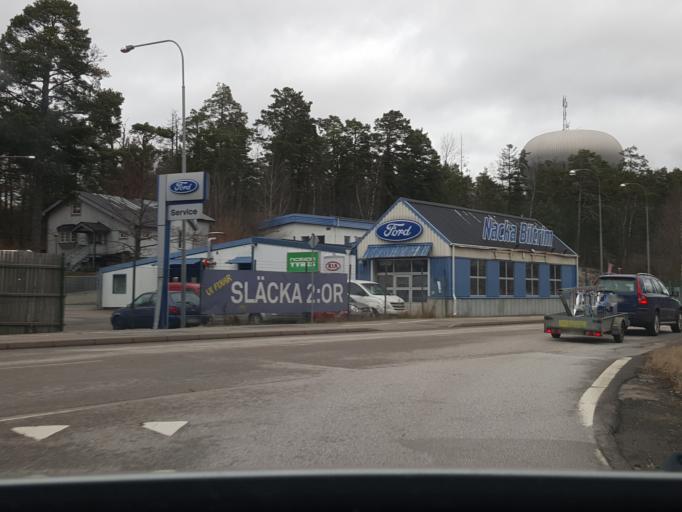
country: SE
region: Stockholm
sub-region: Nacka Kommun
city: Boo
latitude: 59.3227
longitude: 18.2585
